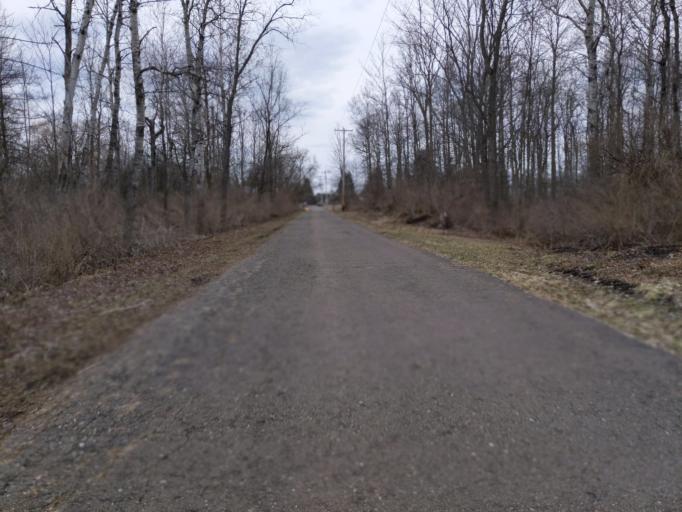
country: US
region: New York
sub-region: Tompkins County
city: Dryden
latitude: 42.5105
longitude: -76.3435
